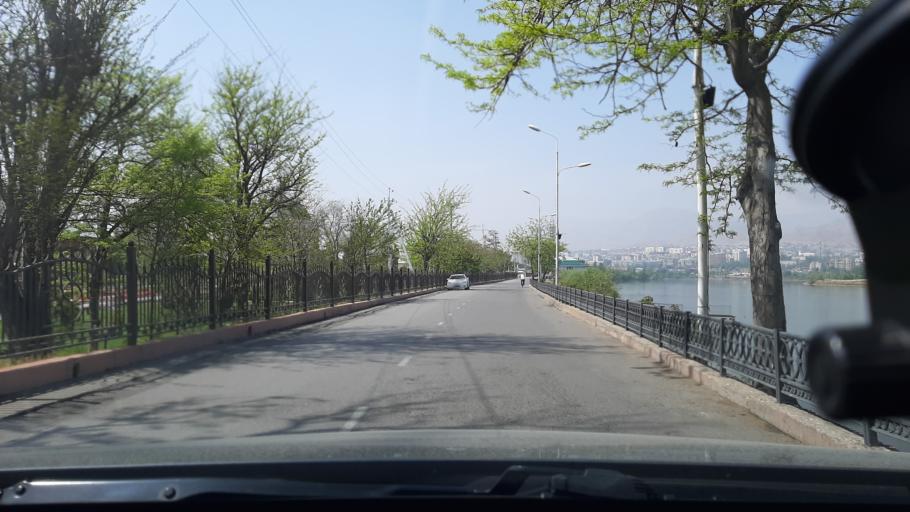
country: TJ
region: Viloyati Sughd
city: Khujand
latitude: 40.2882
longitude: 69.6163
